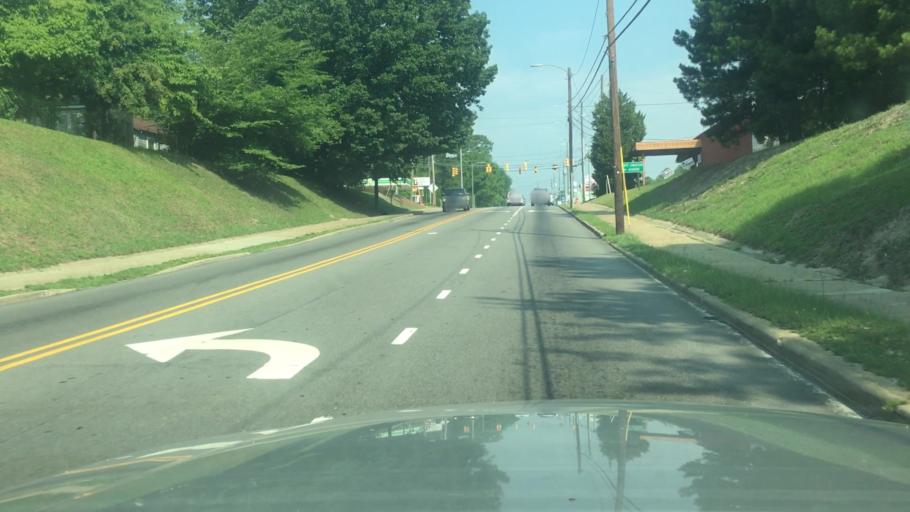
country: US
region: North Carolina
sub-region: Cumberland County
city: Hope Mills
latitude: 34.9750
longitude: -78.9495
